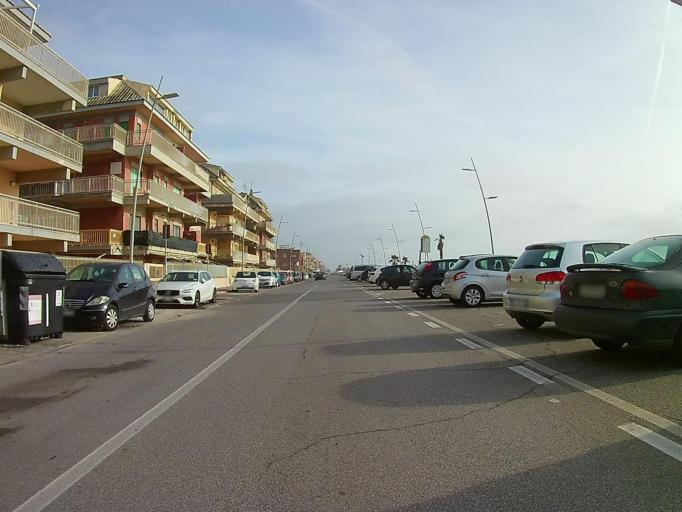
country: IT
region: Latium
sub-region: Citta metropolitana di Roma Capitale
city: Lido di Ostia
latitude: 41.7354
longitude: 12.2592
